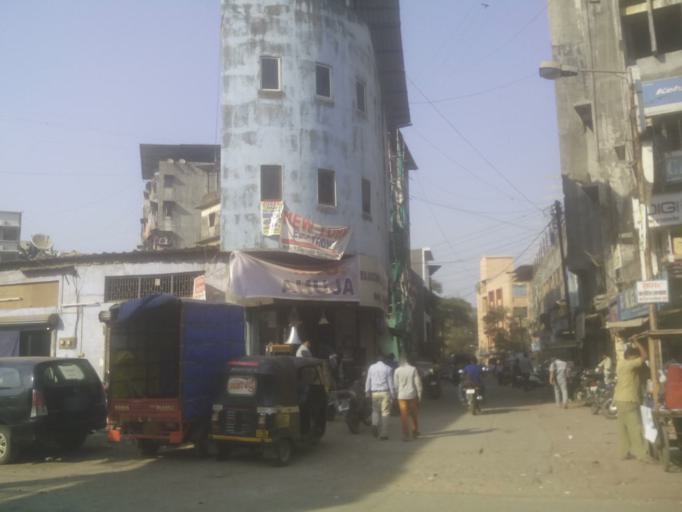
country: IN
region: Maharashtra
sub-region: Thane
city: Ulhasnagar
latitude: 19.2282
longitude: 73.1604
